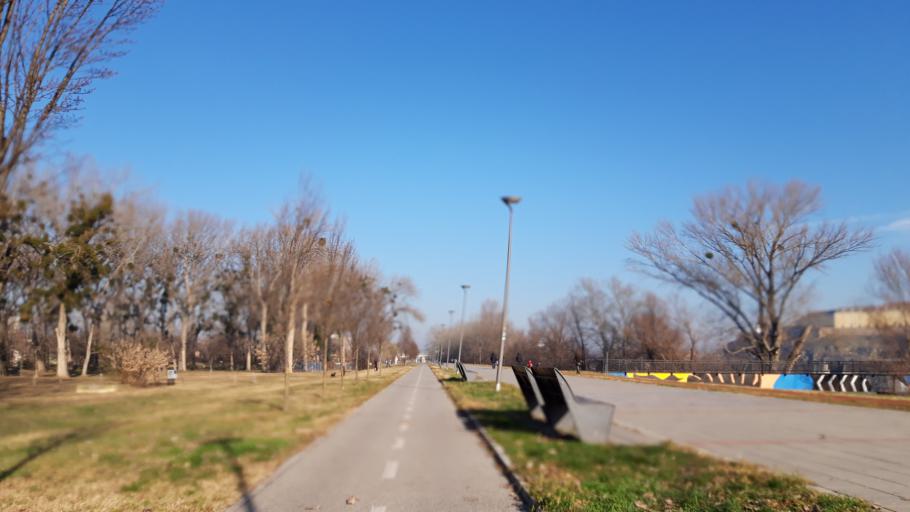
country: RS
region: Autonomna Pokrajina Vojvodina
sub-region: Juznobacki Okrug
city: Novi Sad
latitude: 45.2467
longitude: 19.8554
